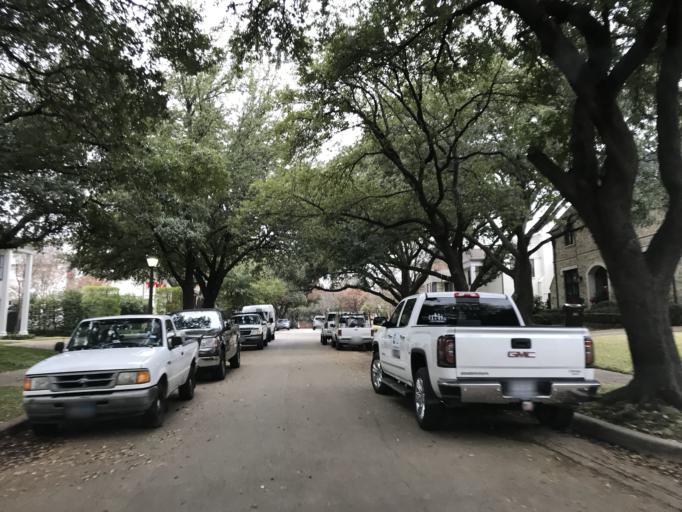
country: US
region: Texas
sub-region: Dallas County
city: Highland Park
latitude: 32.8249
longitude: -96.8138
